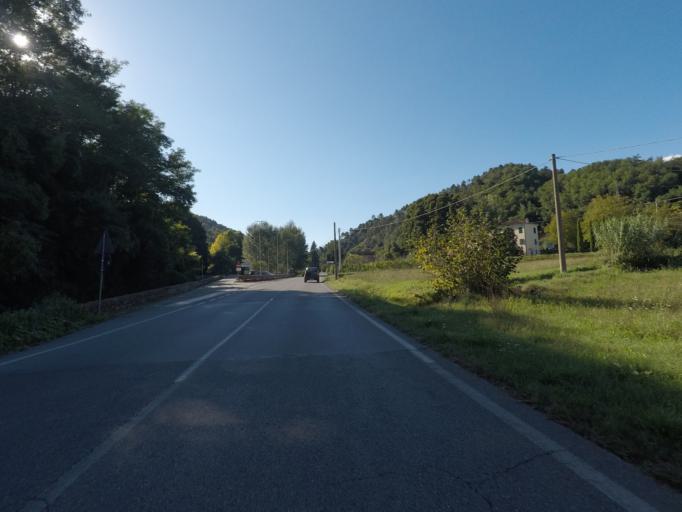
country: IT
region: Tuscany
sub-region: Provincia di Lucca
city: Massarosa
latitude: 43.9004
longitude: 10.3835
